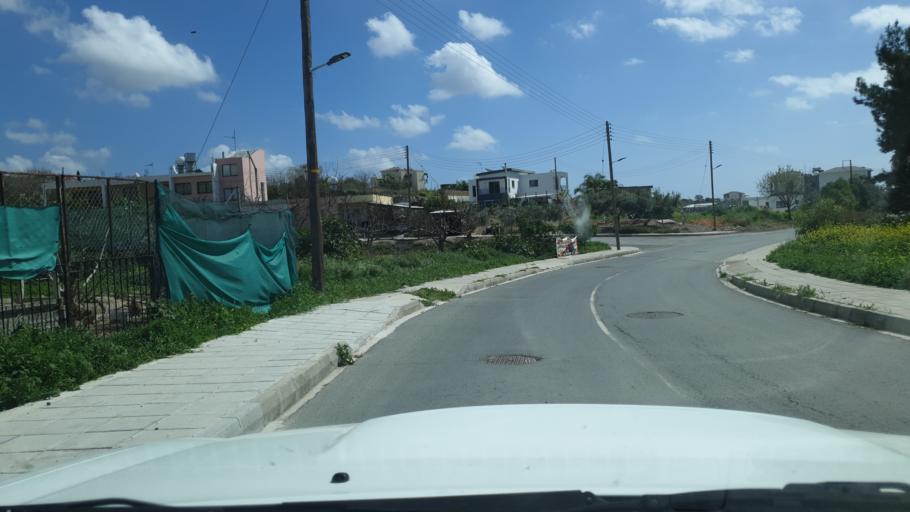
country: CY
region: Pafos
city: Paphos
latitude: 34.7559
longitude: 32.4575
